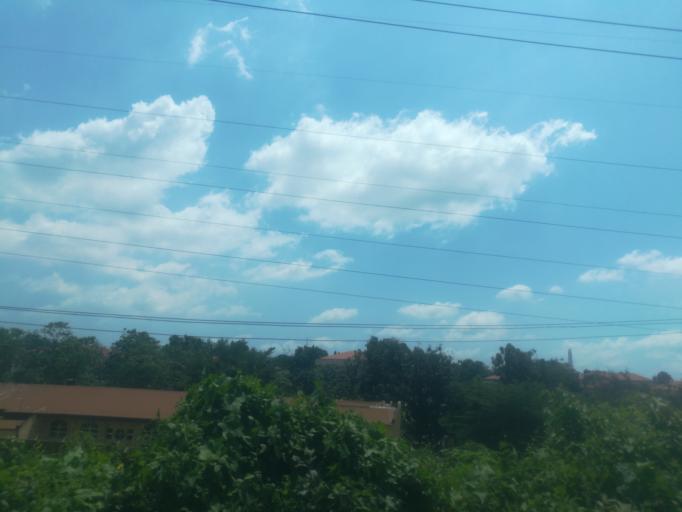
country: NG
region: Oyo
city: Ibadan
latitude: 7.3818
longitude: 3.8685
